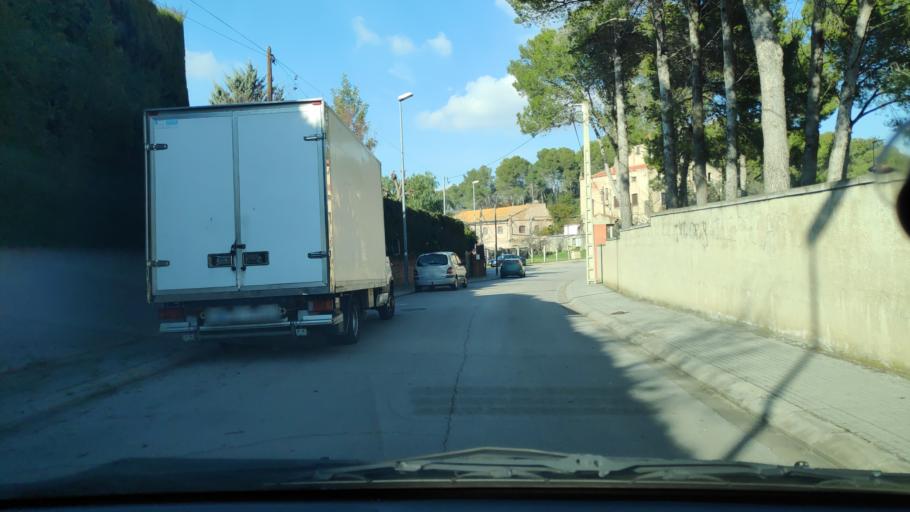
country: ES
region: Catalonia
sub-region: Provincia de Barcelona
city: Sant Quirze del Valles
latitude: 41.5077
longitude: 2.0898
